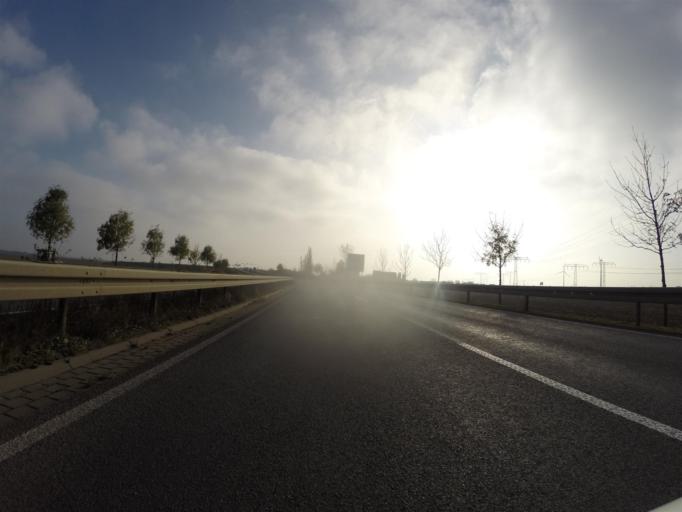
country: DE
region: Saxony
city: Markranstadt
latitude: 51.2661
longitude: 12.2669
